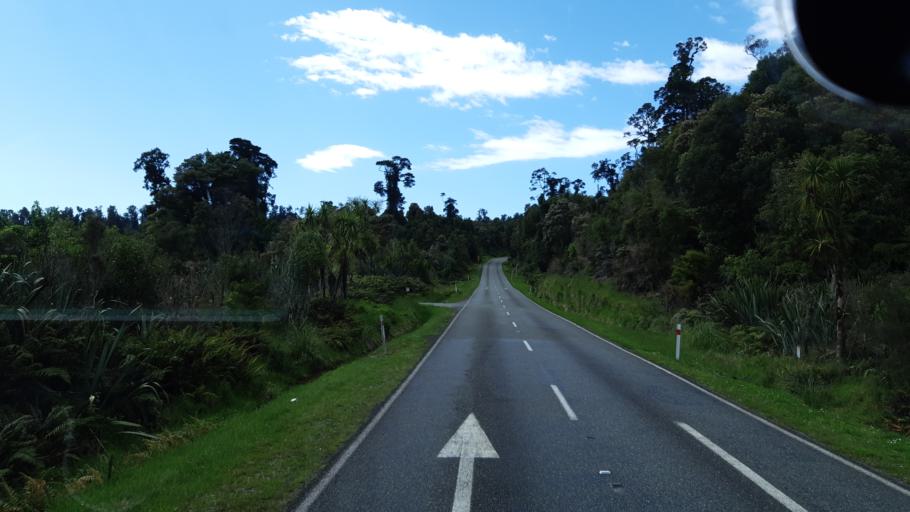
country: NZ
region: West Coast
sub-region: Westland District
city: Hokitika
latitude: -43.0504
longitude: 170.6379
